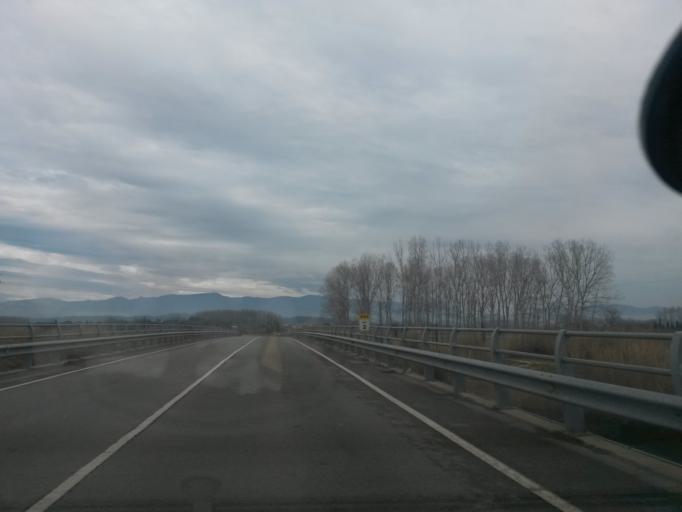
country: ES
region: Catalonia
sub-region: Provincia de Girona
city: Cabanes
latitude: 42.2987
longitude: 2.9780
